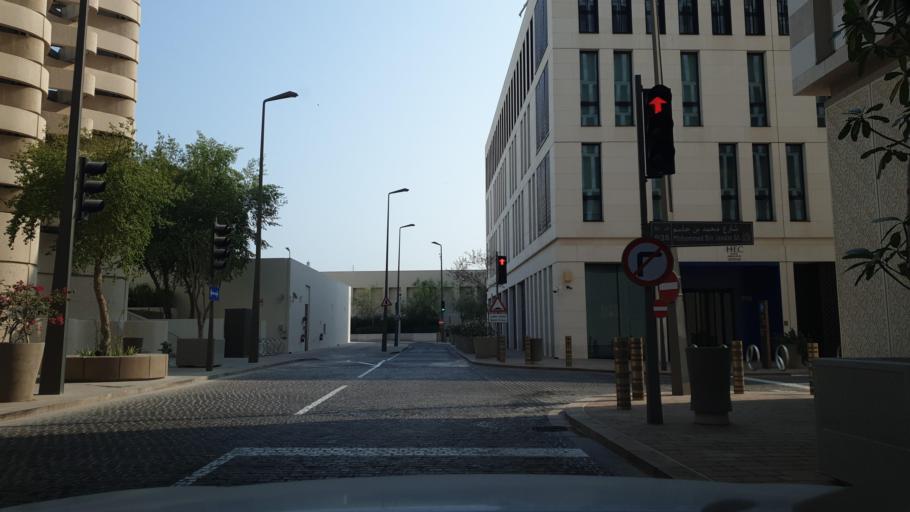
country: QA
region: Baladiyat ad Dawhah
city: Doha
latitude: 25.2859
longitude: 51.5292
